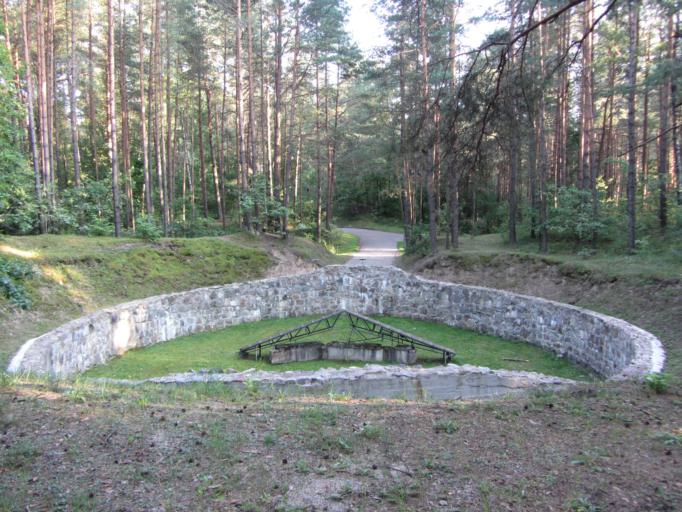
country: LT
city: Baltoji Voke
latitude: 54.6263
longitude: 25.1629
